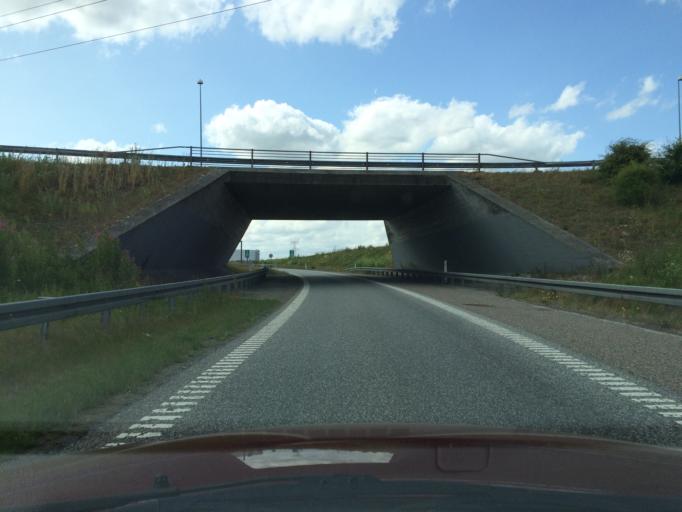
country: DK
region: Central Jutland
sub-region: Arhus Kommune
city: Kolt
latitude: 56.1571
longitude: 10.0696
